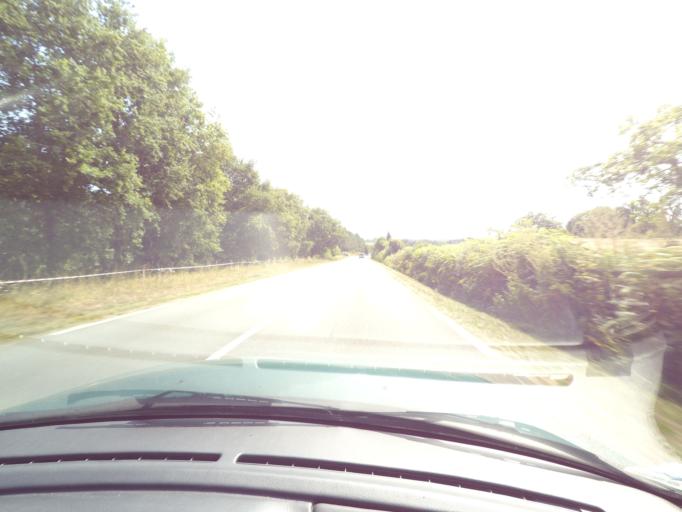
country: FR
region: Limousin
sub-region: Departement de la Haute-Vienne
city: Feytiat
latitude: 45.8078
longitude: 1.3533
